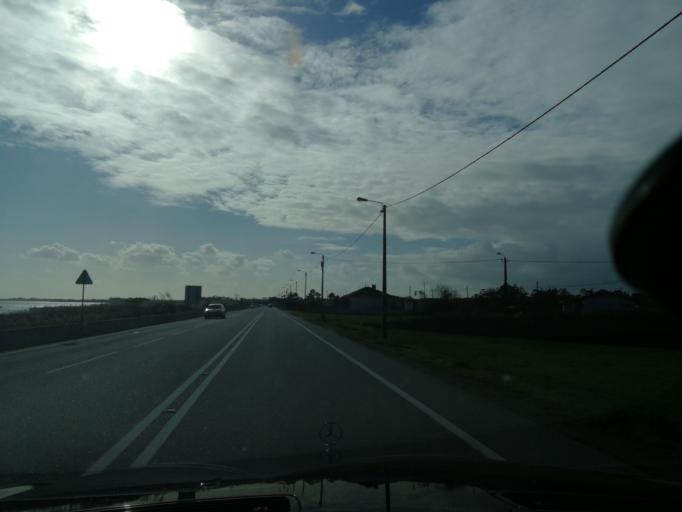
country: PT
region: Aveiro
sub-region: Estarreja
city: Pardilho
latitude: 40.7872
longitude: -8.6816
